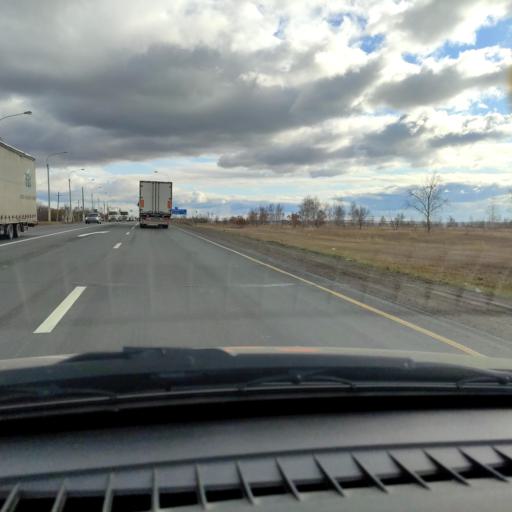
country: RU
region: Samara
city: Syzran'
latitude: 53.2101
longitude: 48.5012
